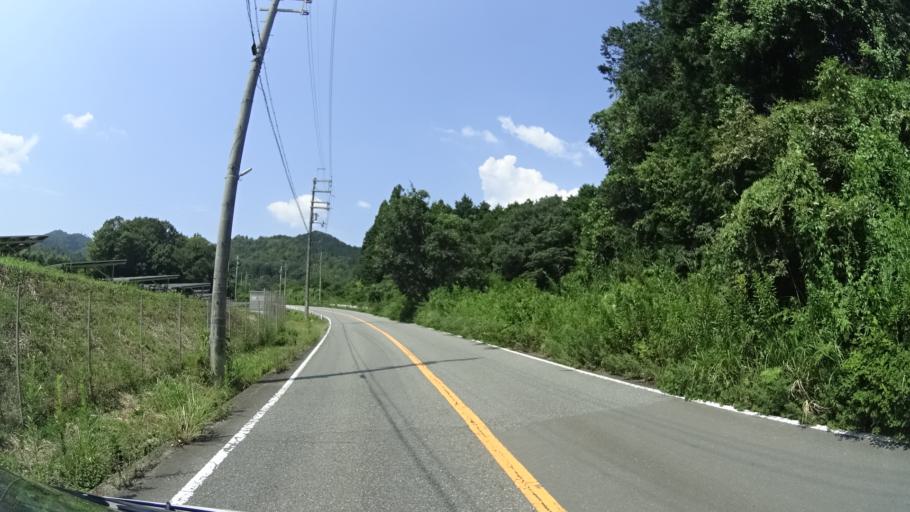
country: JP
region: Kyoto
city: Fukuchiyama
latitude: 35.2565
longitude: 135.1476
